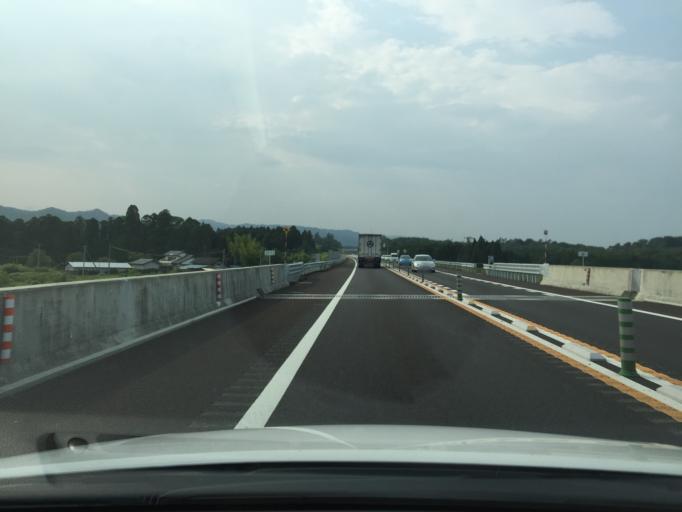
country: JP
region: Fukushima
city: Namie
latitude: 37.4859
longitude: 140.9524
